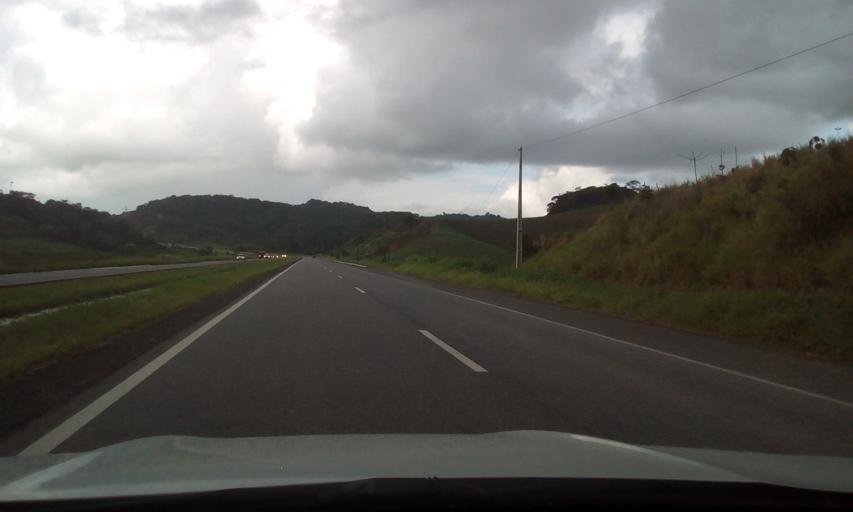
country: BR
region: Pernambuco
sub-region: Cabo De Santo Agostinho
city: Cabo
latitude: -8.2571
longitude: -35.0401
